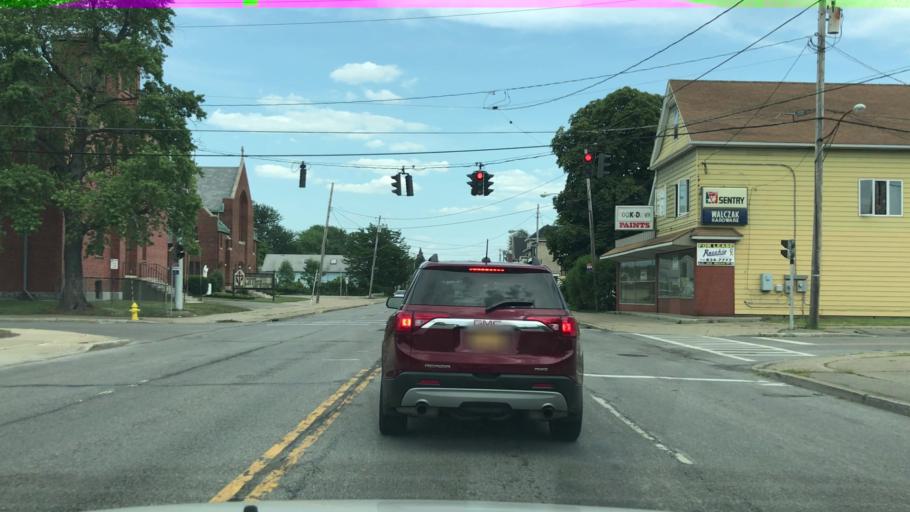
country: US
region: New York
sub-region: Erie County
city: Sloan
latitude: 42.8843
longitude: -78.7817
